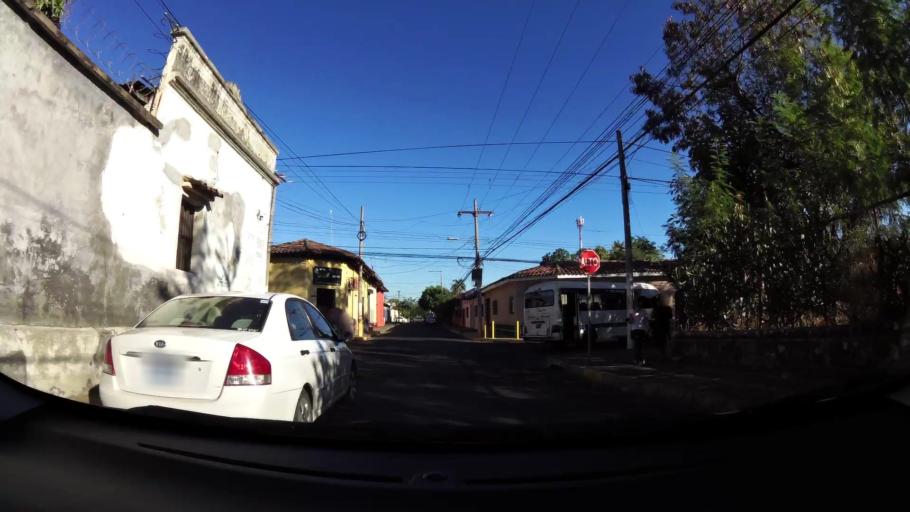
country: SV
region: San Miguel
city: San Miguel
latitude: 13.4831
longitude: -88.1833
